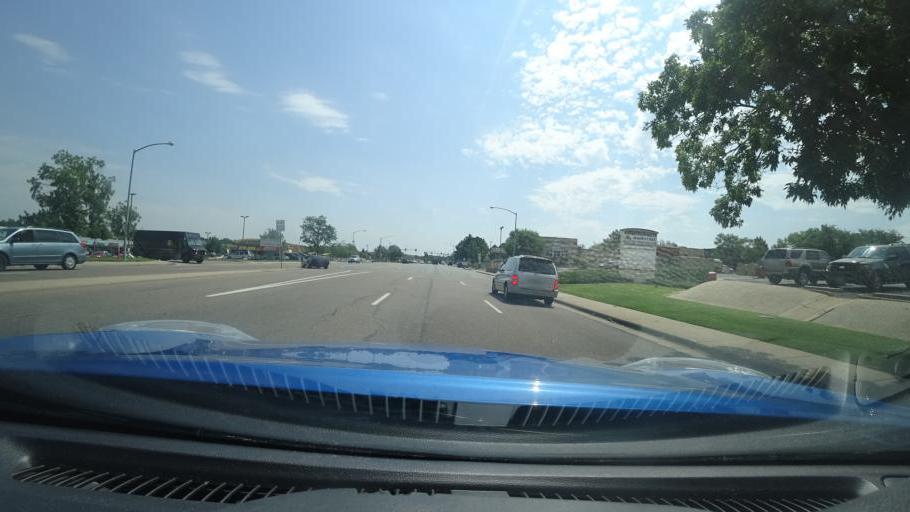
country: US
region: Colorado
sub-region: Adams County
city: Aurora
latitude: 39.6736
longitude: -104.7933
